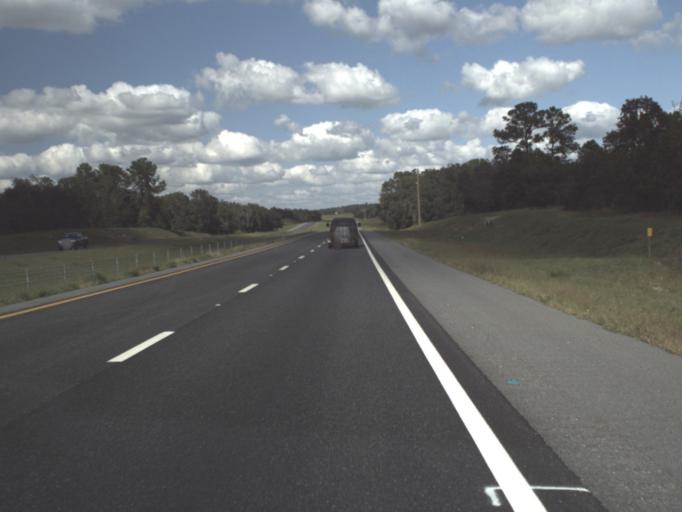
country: US
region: Florida
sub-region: Hernando County
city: Brookridge
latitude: 28.5705
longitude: -82.4800
